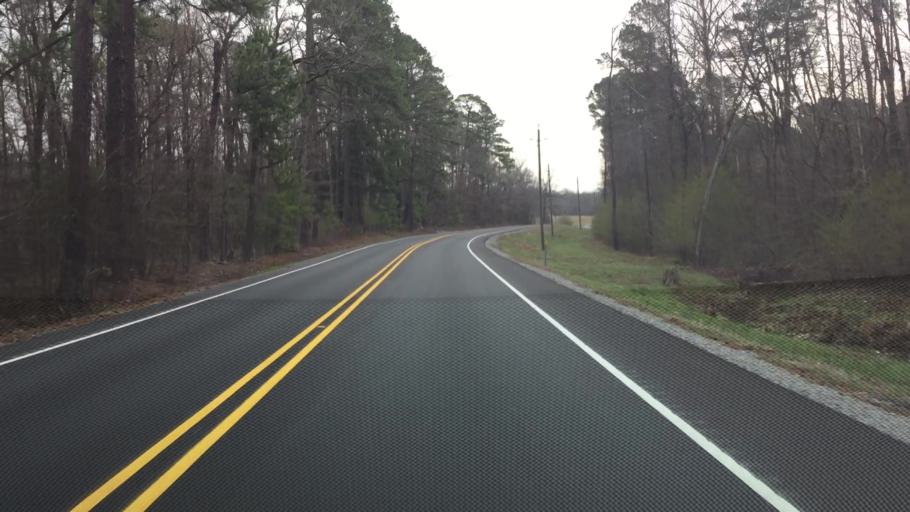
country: US
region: Arkansas
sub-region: Saline County
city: Haskell
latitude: 34.6160
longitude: -92.7863
